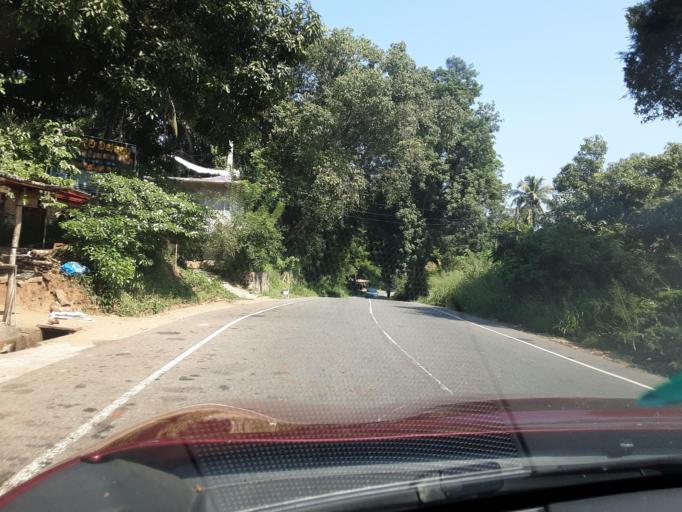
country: LK
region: Uva
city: Badulla
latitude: 7.1609
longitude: 81.0516
